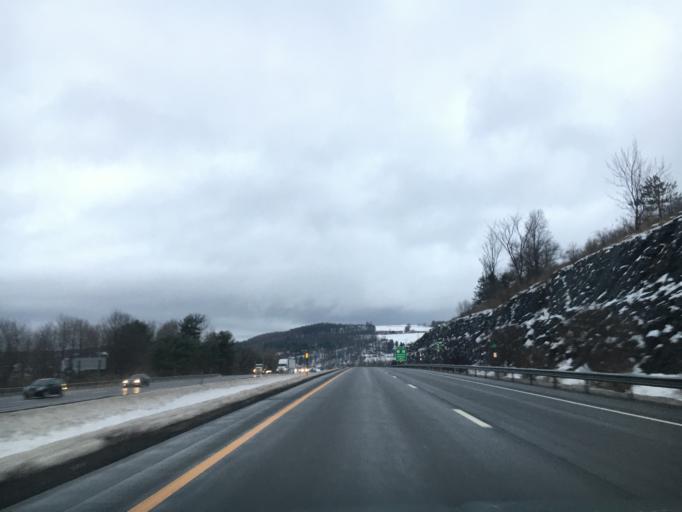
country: US
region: New York
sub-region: Cortland County
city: McGraw
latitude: 42.5810
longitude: -76.1239
